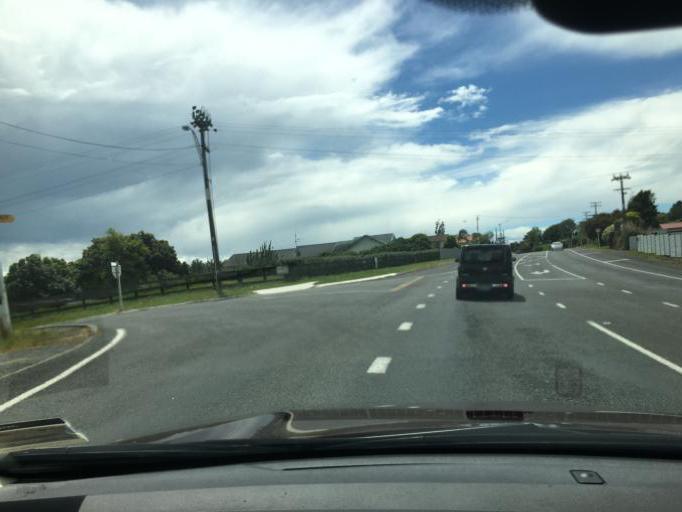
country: NZ
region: Waikato
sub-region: Waipa District
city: Cambridge
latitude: -37.9283
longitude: 175.3100
